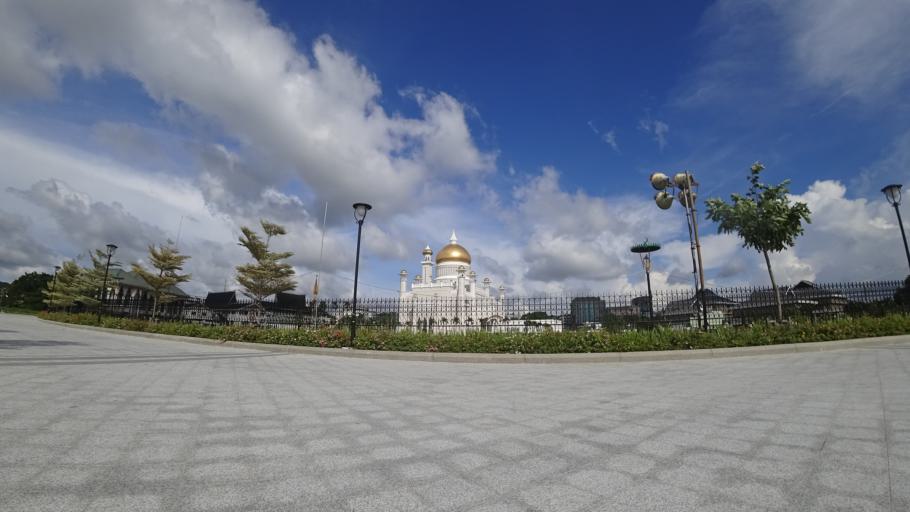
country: BN
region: Brunei and Muara
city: Bandar Seri Begawan
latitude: 4.8892
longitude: 114.9378
